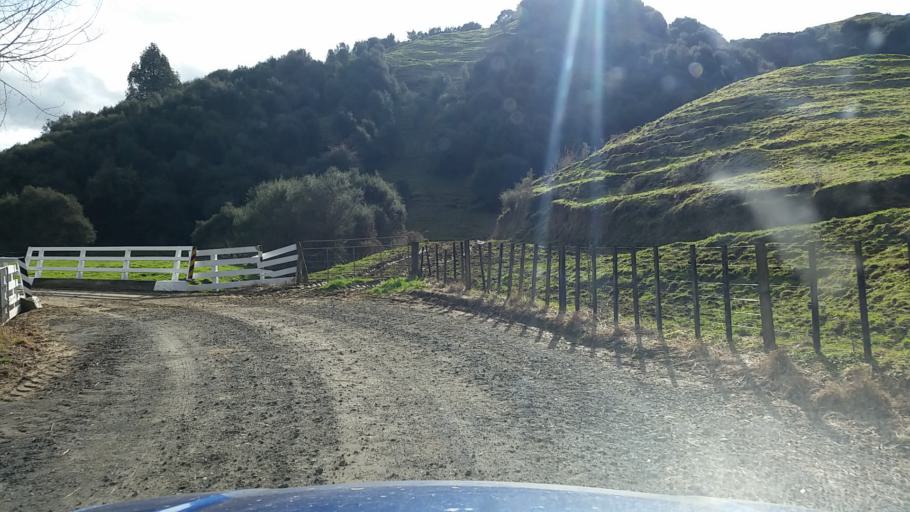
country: NZ
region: Taranaki
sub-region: South Taranaki District
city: Eltham
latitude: -39.2605
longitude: 174.5805
